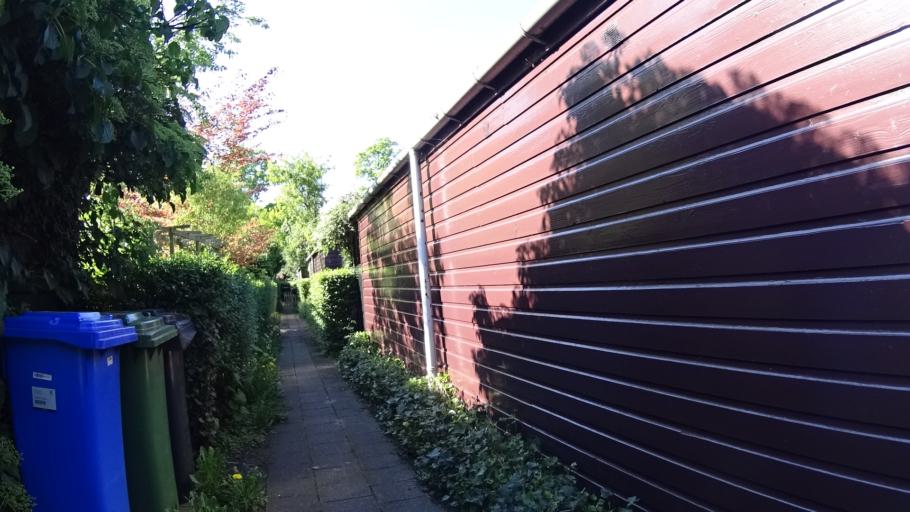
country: NL
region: South Holland
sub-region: Gemeente Delft
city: Delft
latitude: 52.0162
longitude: 4.3449
